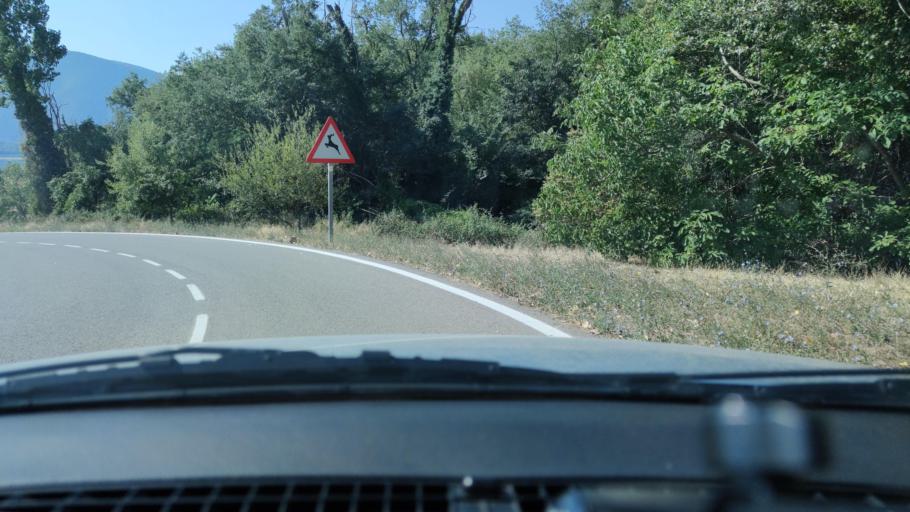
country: ES
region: Catalonia
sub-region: Provincia de Lleida
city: Tremp
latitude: 42.2274
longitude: 0.9591
